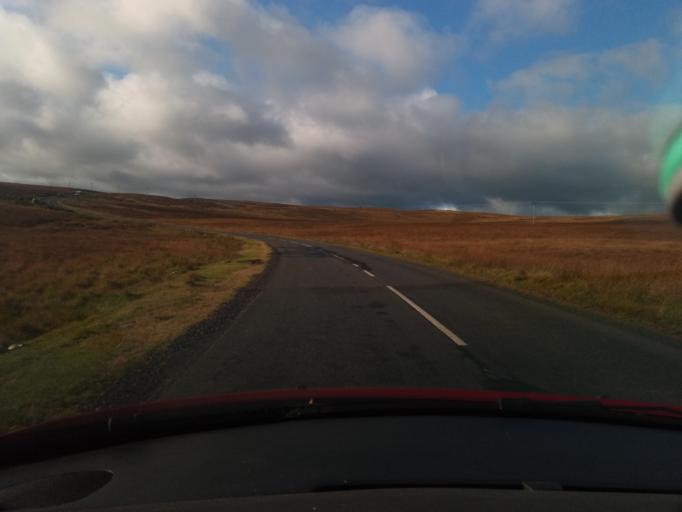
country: GB
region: Scotland
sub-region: The Scottish Borders
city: Lauder
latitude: 55.7098
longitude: -2.7937
